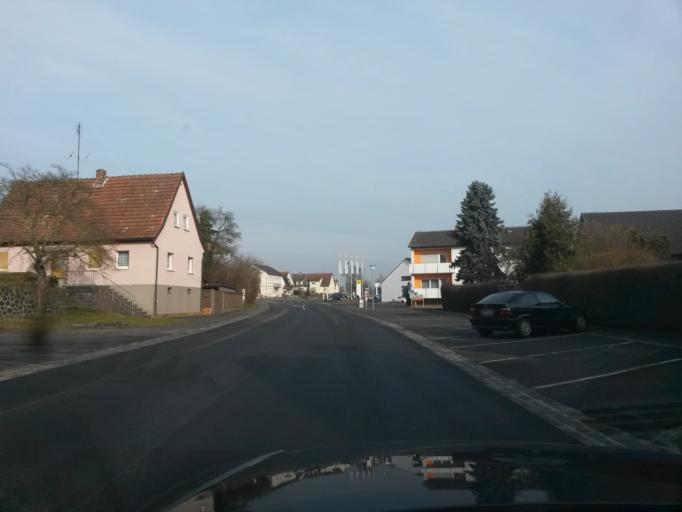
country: DE
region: Bavaria
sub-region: Regierungsbezirk Unterfranken
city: Sondheim vor der Rhoen
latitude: 50.4793
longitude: 10.1809
